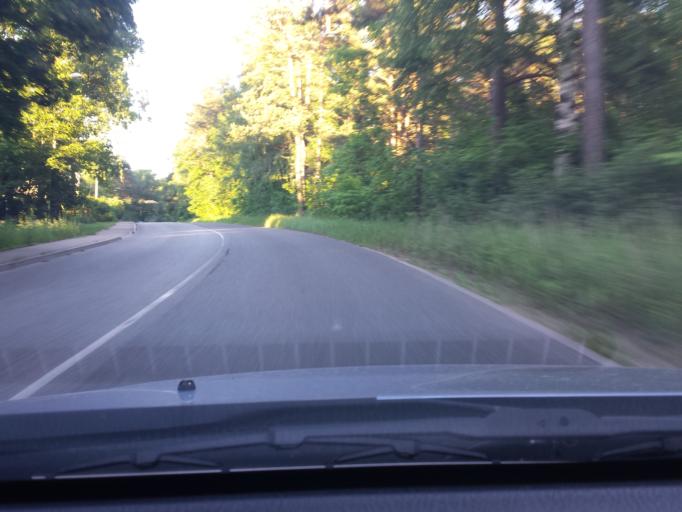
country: LV
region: Riga
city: Jaunciems
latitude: 57.0366
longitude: 24.1796
